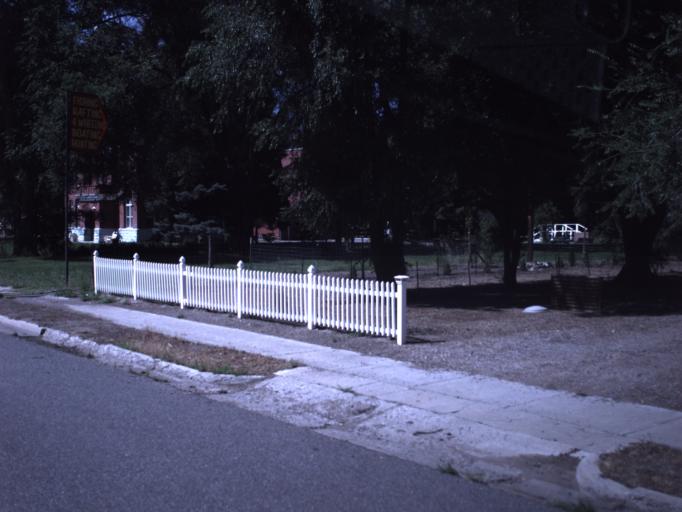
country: US
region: Utah
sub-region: Piute County
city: Junction
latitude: 38.2380
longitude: -112.2200
